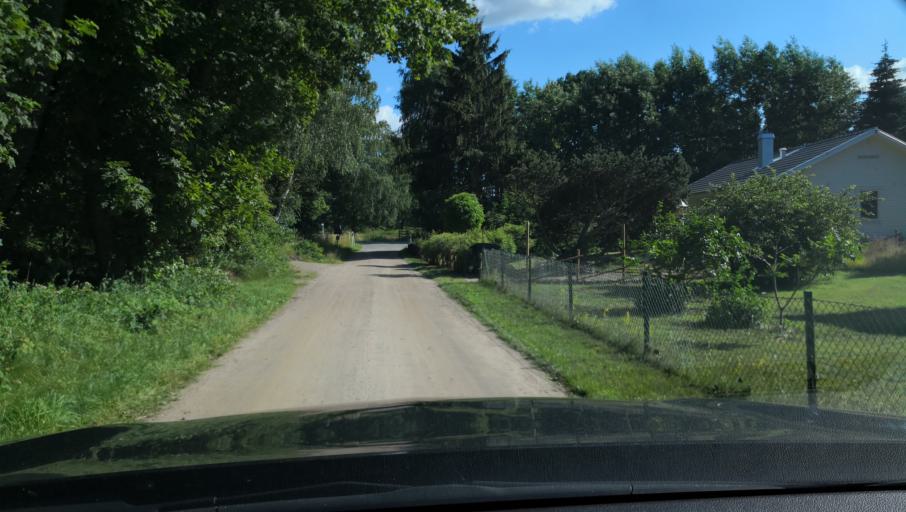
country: SE
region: Skane
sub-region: Simrishamns Kommun
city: Kivik
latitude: 55.7905
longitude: 14.1956
